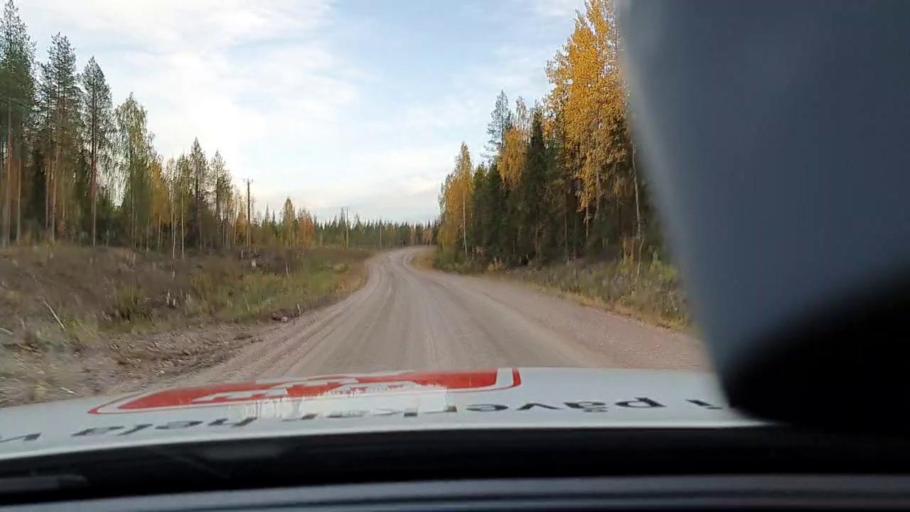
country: SE
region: Norrbotten
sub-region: Overkalix Kommun
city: OEverkalix
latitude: 66.3229
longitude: 22.6311
